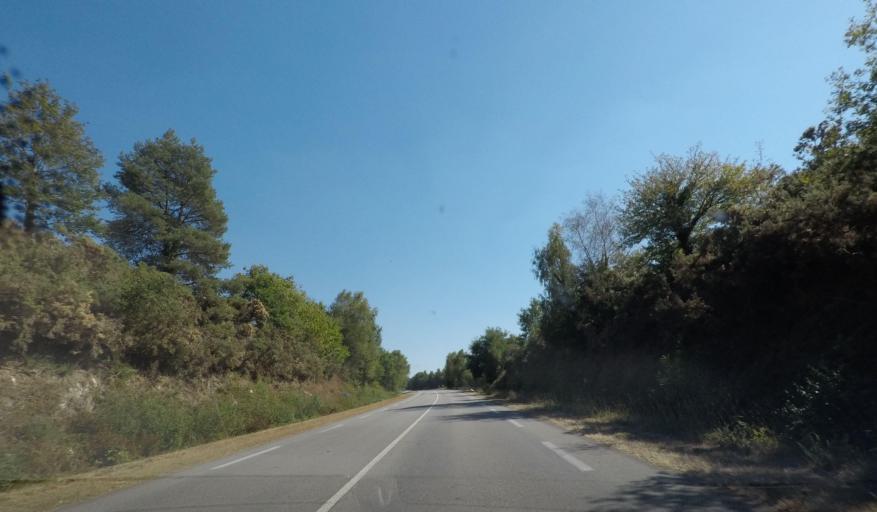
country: FR
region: Brittany
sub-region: Departement du Morbihan
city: Questembert
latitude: 47.6506
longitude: -2.4290
